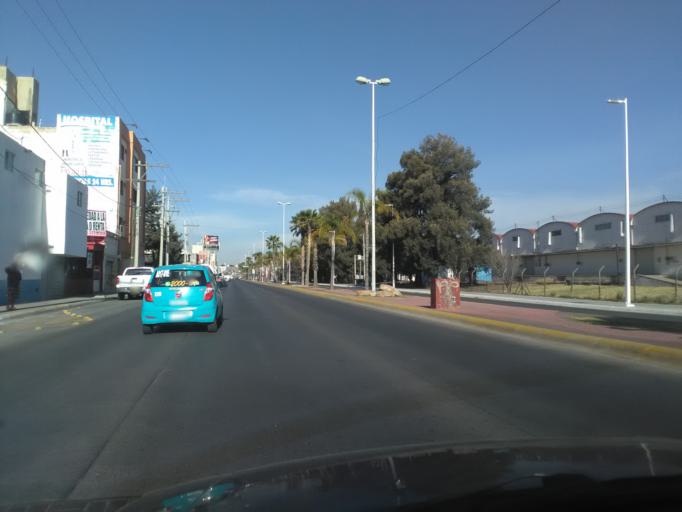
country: MX
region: Durango
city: Victoria de Durango
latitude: 24.0354
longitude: -104.6626
